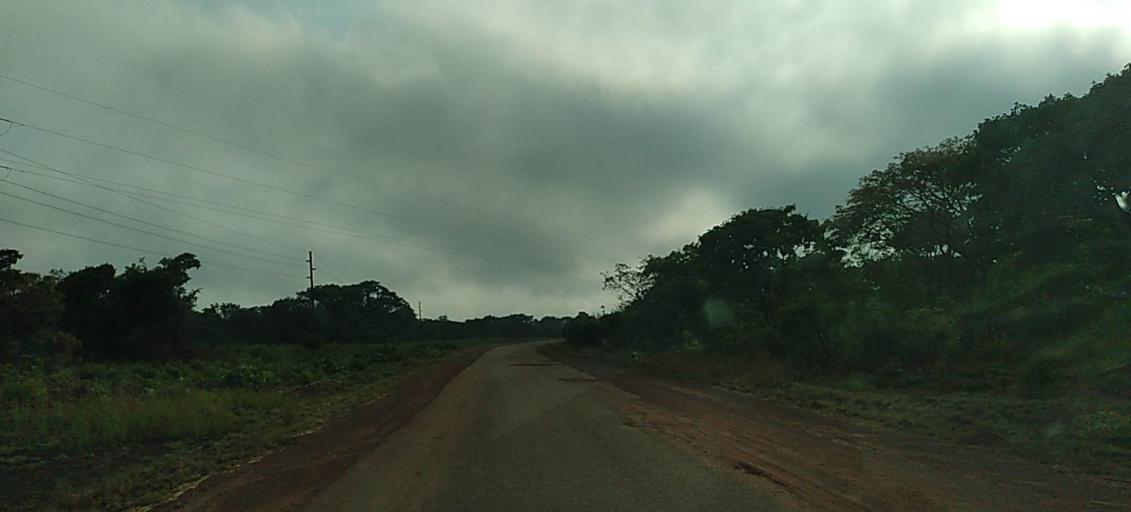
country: ZM
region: North-Western
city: Mwinilunga
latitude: -11.7257
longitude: 24.4946
